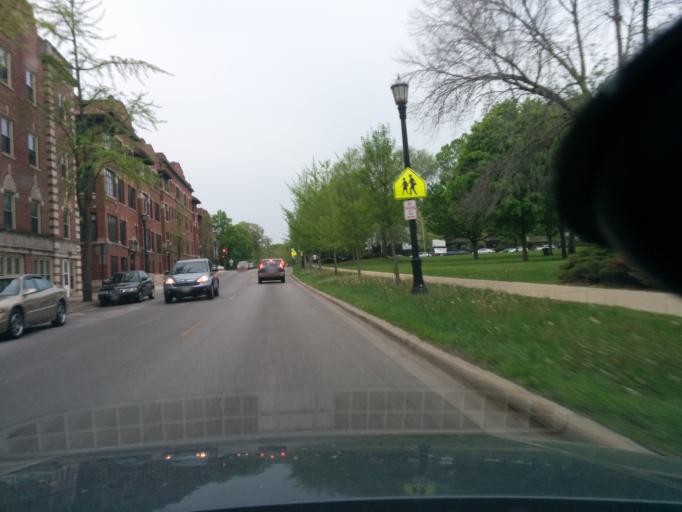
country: US
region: Illinois
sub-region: Cook County
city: Evanston
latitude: 42.0341
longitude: -87.6854
